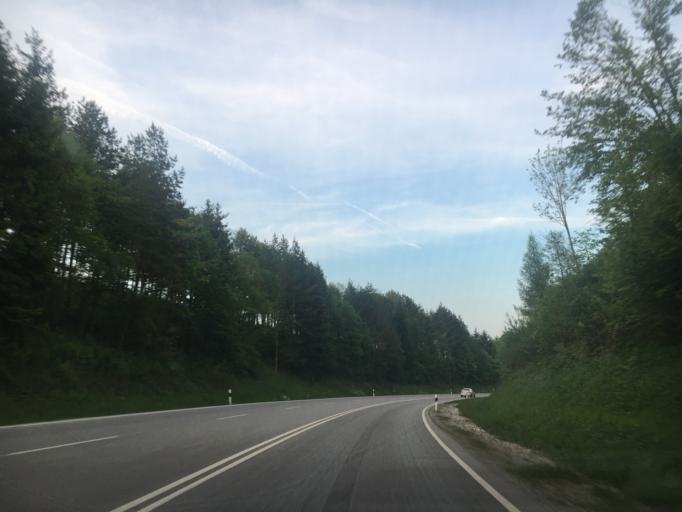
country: DE
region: Bavaria
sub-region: Upper Bavaria
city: Bad Toelz
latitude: 47.7552
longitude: 11.5416
